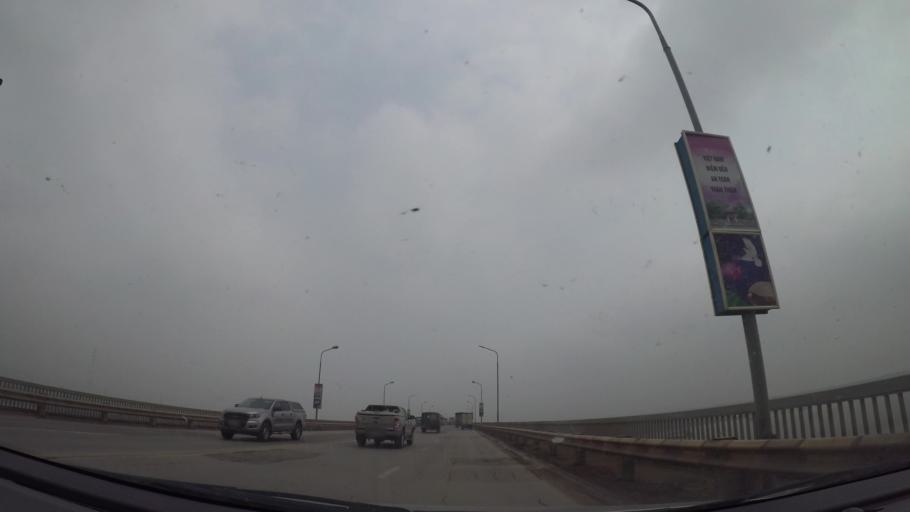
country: VN
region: Ha Noi
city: Tay Ho
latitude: 21.0961
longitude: 105.7863
